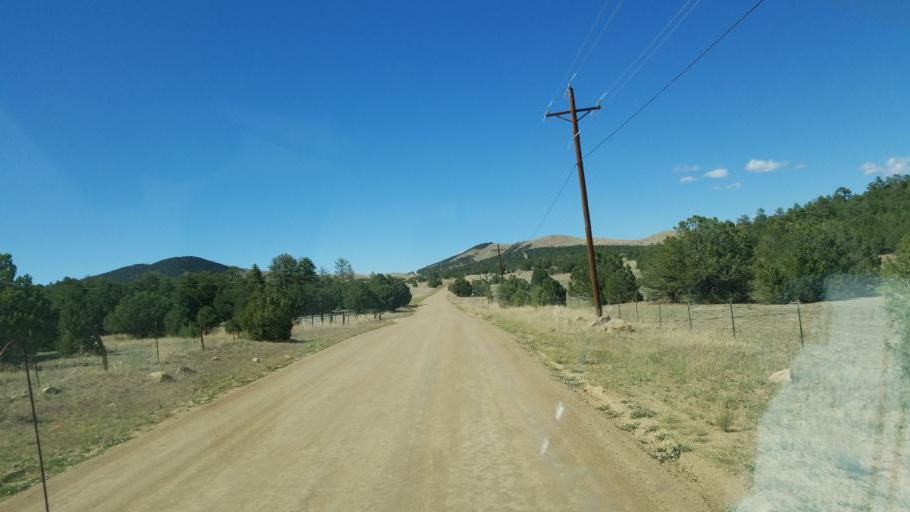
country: US
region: Colorado
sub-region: Custer County
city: Westcliffe
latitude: 38.3011
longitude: -105.4865
